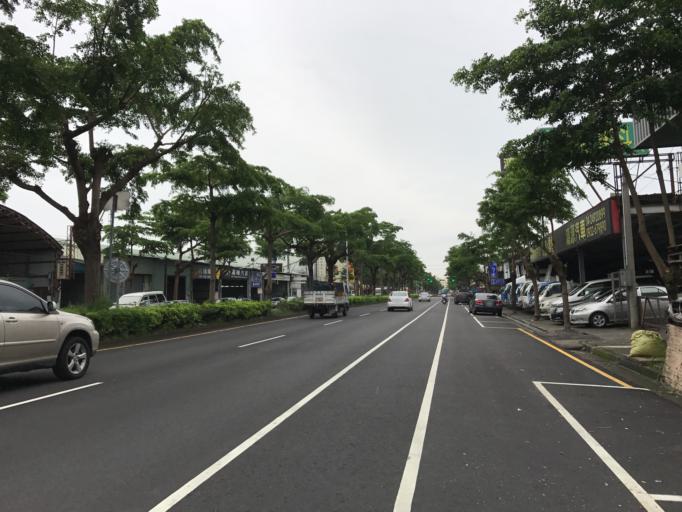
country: TW
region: Taiwan
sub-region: Taichung City
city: Taichung
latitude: 24.0814
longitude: 120.6886
